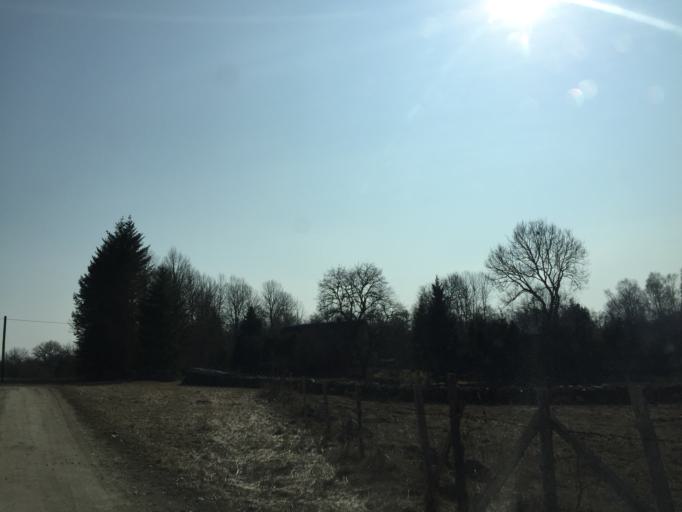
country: EE
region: Saare
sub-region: Orissaare vald
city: Orissaare
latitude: 58.4798
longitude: 23.1221
